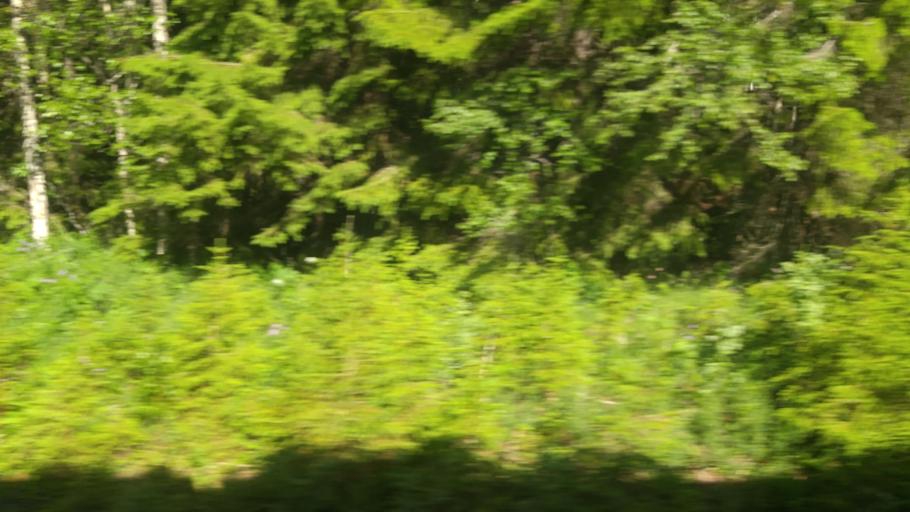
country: SE
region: Jaemtland
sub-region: Are Kommun
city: Are
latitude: 63.3855
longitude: 12.8919
